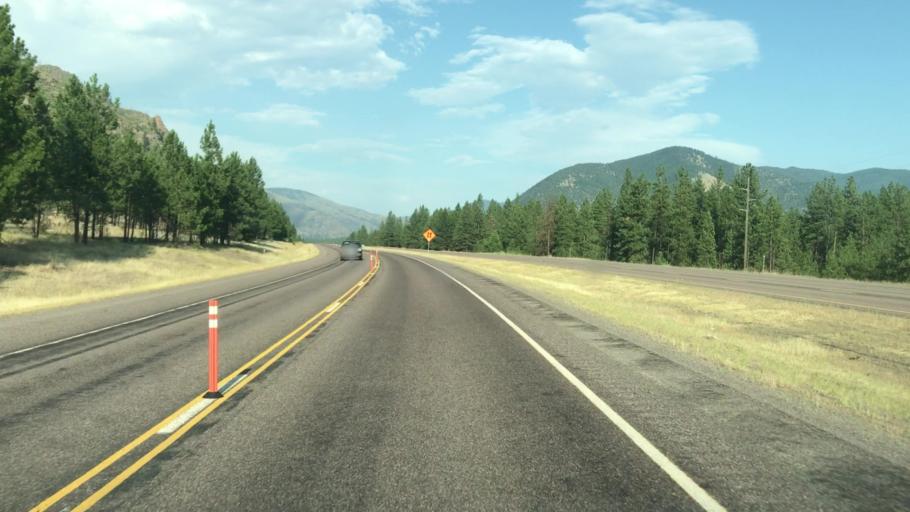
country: US
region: Montana
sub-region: Mineral County
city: Superior
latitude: 47.0117
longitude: -114.7199
